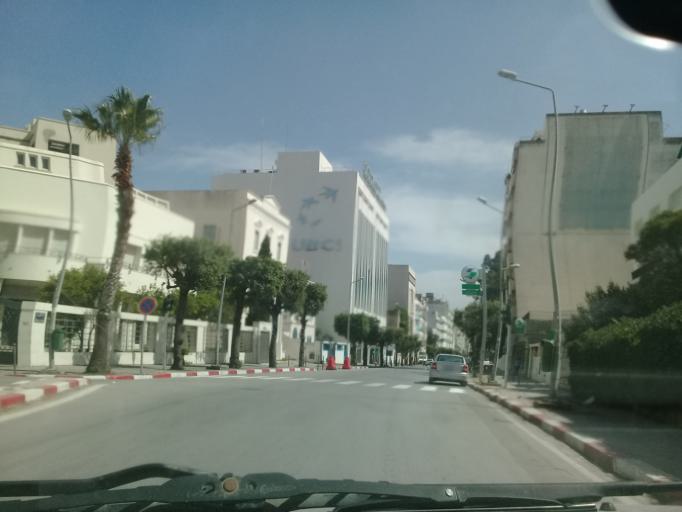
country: TN
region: Tunis
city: Tunis
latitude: 36.8203
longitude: 10.1780
